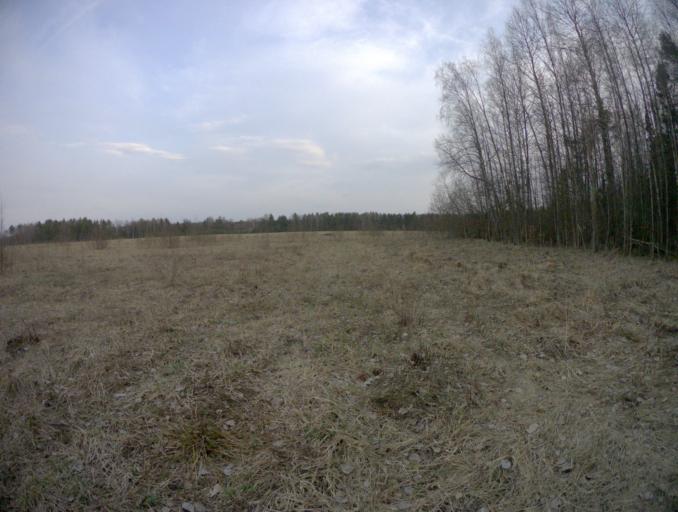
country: RU
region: Vladimir
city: Kommunar
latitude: 56.0775
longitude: 40.5284
